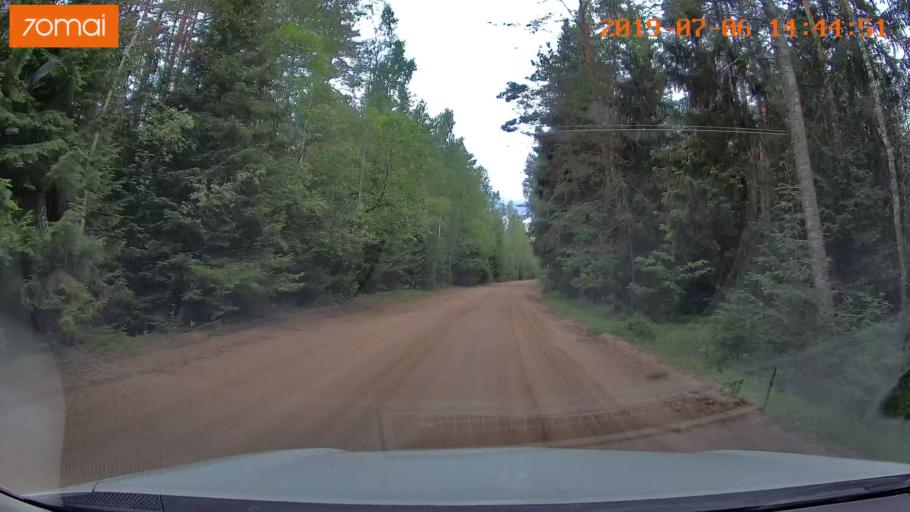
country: BY
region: Minsk
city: Ivyanyets
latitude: 53.9662
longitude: 26.6906
